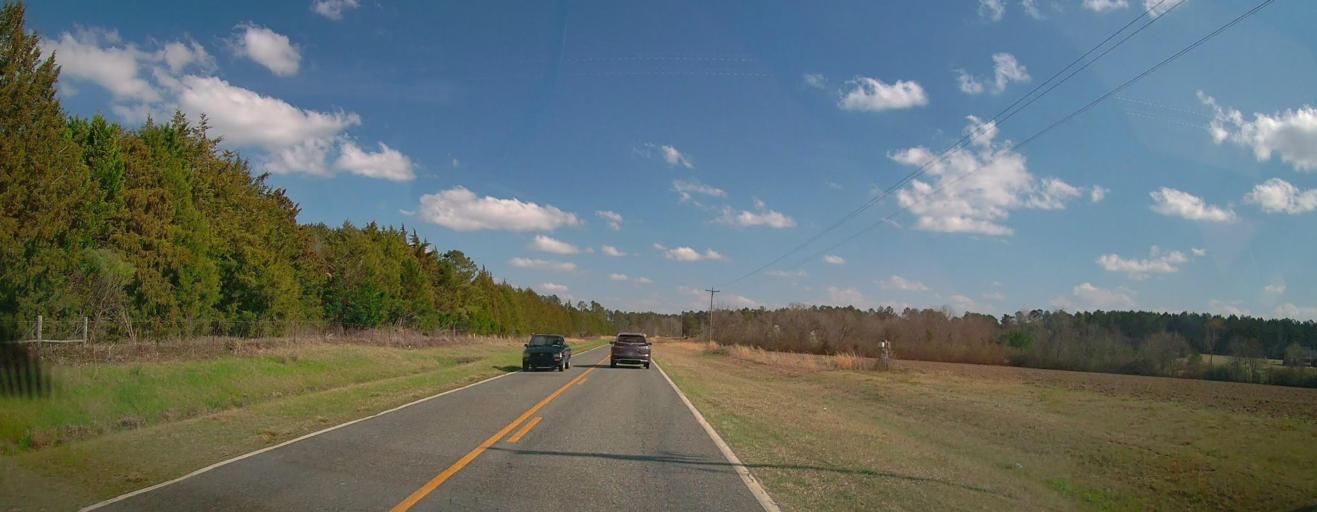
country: US
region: Georgia
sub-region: Laurens County
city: Dublin
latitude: 32.5880
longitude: -83.0605
